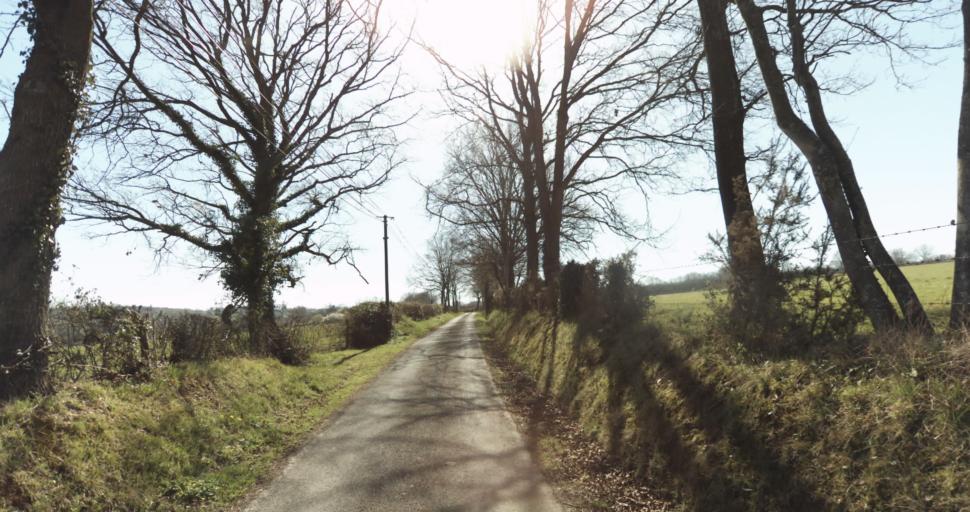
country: FR
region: Lower Normandy
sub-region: Departement du Calvados
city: Livarot
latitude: 49.0080
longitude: 0.0842
